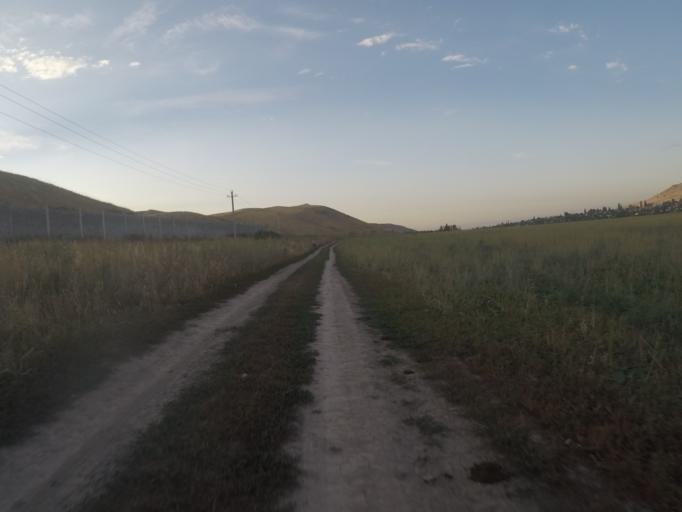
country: KG
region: Chuy
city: Bishkek
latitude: 42.7583
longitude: 74.6361
